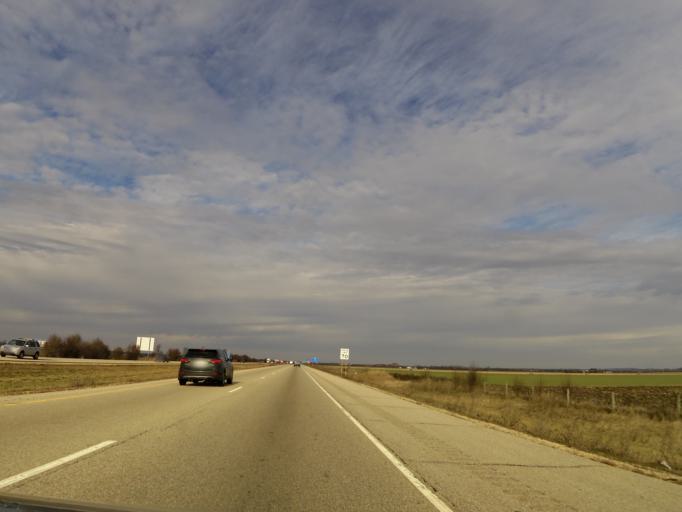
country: US
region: Wisconsin
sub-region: Rock County
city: Janesville
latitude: 42.6448
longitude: -88.9829
